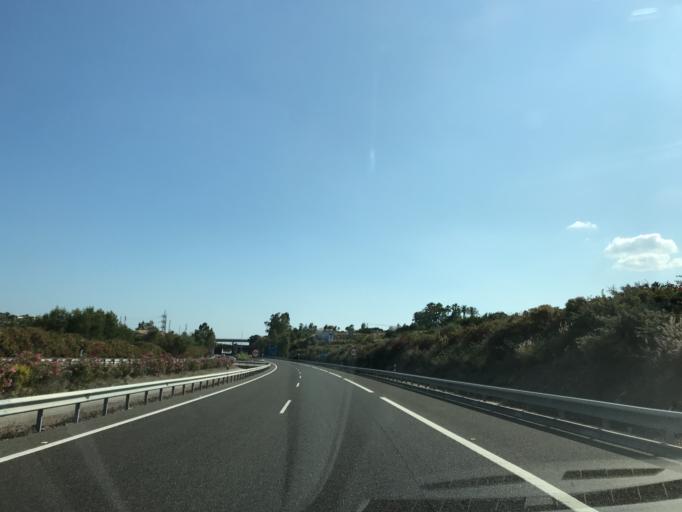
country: ES
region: Andalusia
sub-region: Provincia de Malaga
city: Benahavis
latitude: 36.5114
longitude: -4.9906
